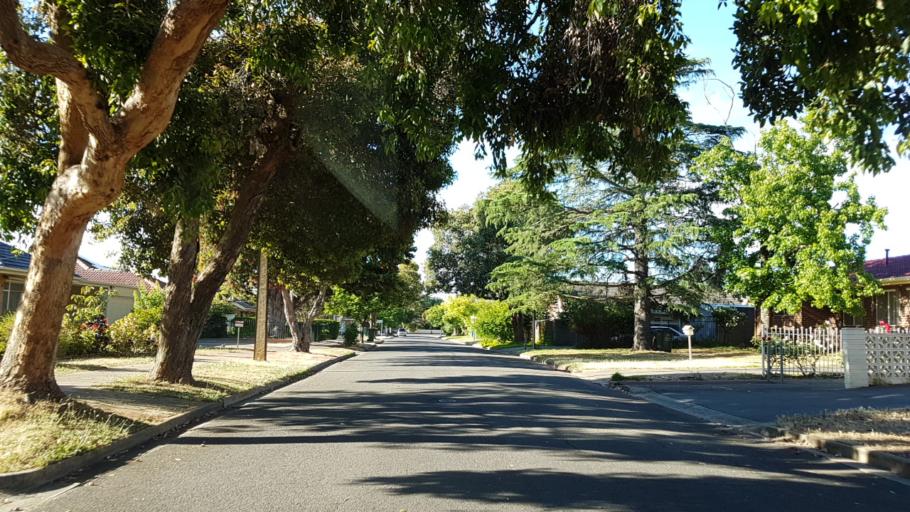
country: AU
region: South Australia
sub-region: Campbelltown
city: Campbelltown
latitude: -34.8899
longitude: 138.6789
